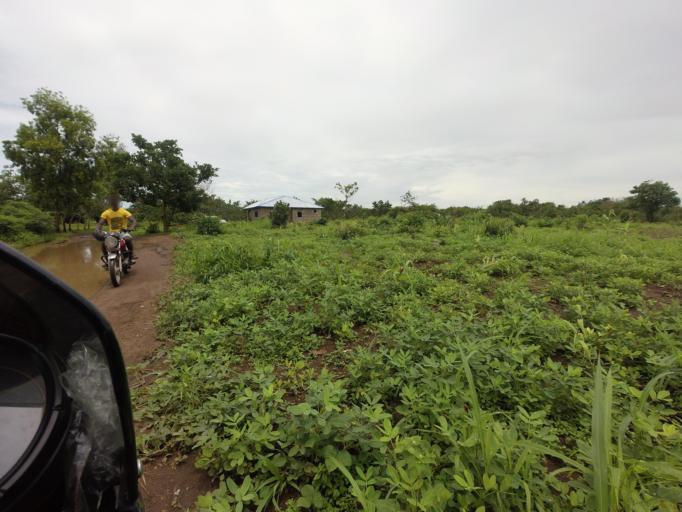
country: SL
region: Northern Province
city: Kambia
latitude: 9.1055
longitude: -12.9305
